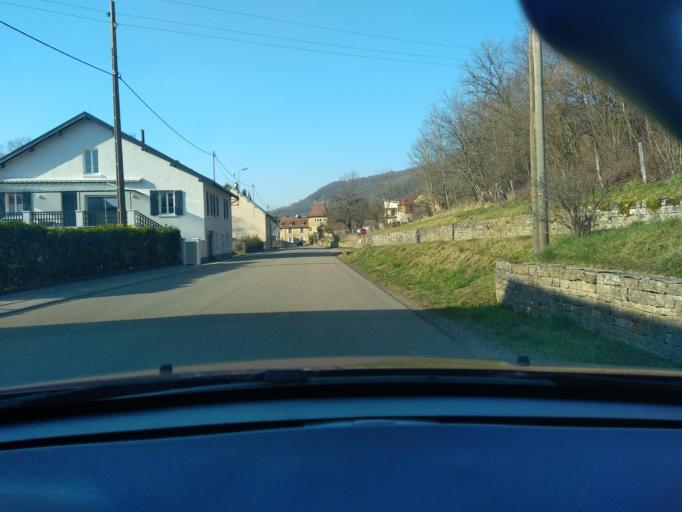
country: FR
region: Franche-Comte
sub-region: Departement du Jura
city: Perrigny
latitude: 46.6515
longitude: 5.6009
